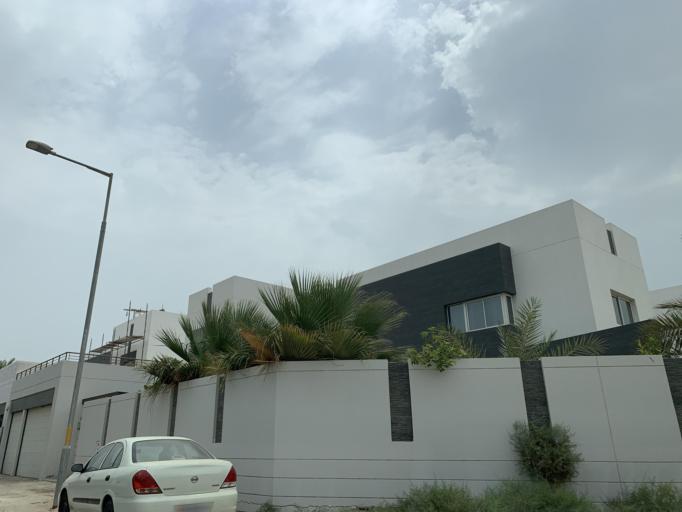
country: BH
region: Central Governorate
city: Madinat Hamad
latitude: 26.1791
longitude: 50.4745
